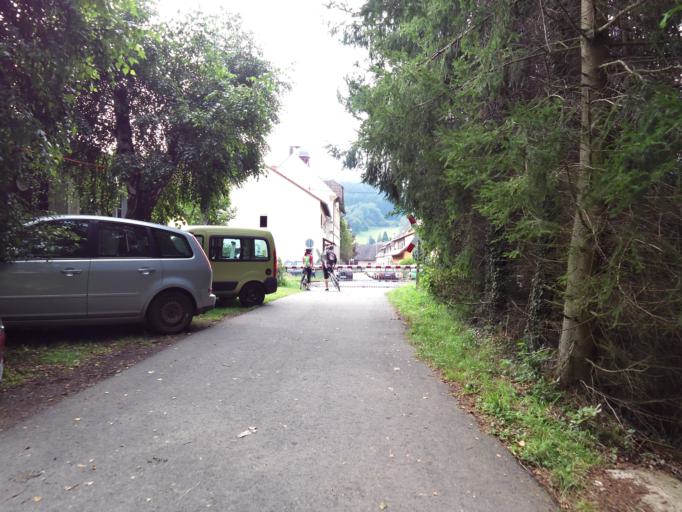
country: DE
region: Rheinland-Pfalz
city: Bayerfeld-Steckweiler
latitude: 49.6756
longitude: 7.8047
